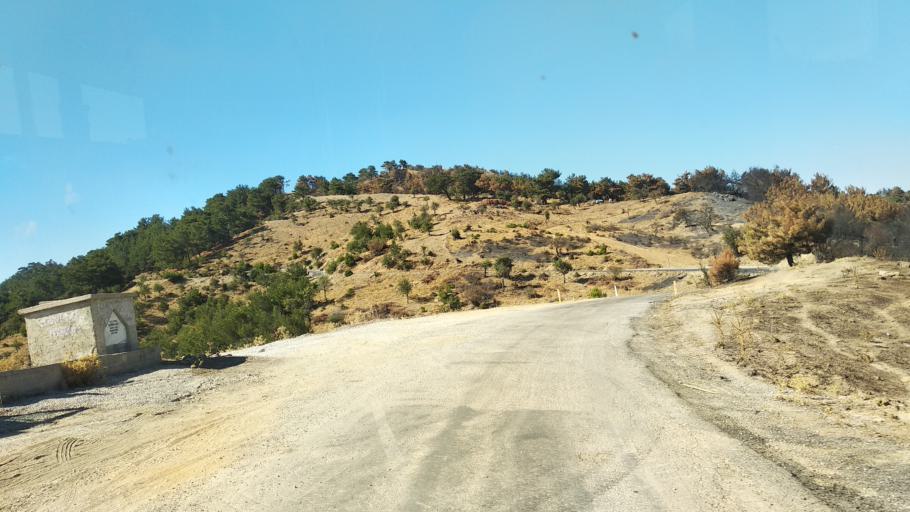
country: TR
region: Izmir
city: Gaziemir
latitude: 38.2936
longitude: 27.0013
